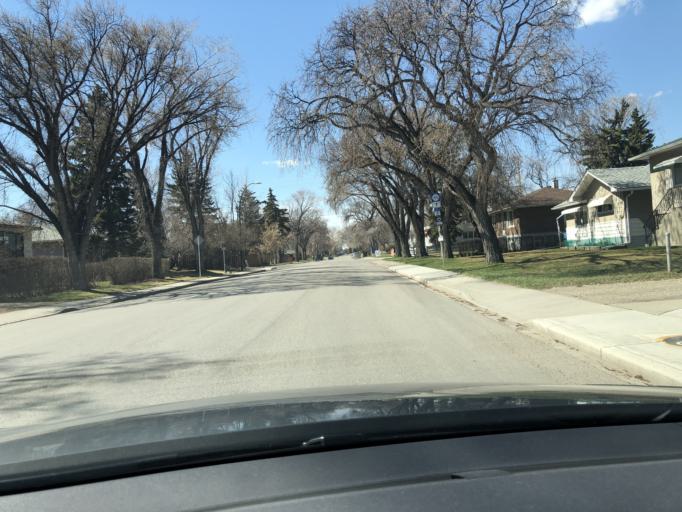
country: CA
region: Alberta
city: Calgary
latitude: 50.9977
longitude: -114.0136
